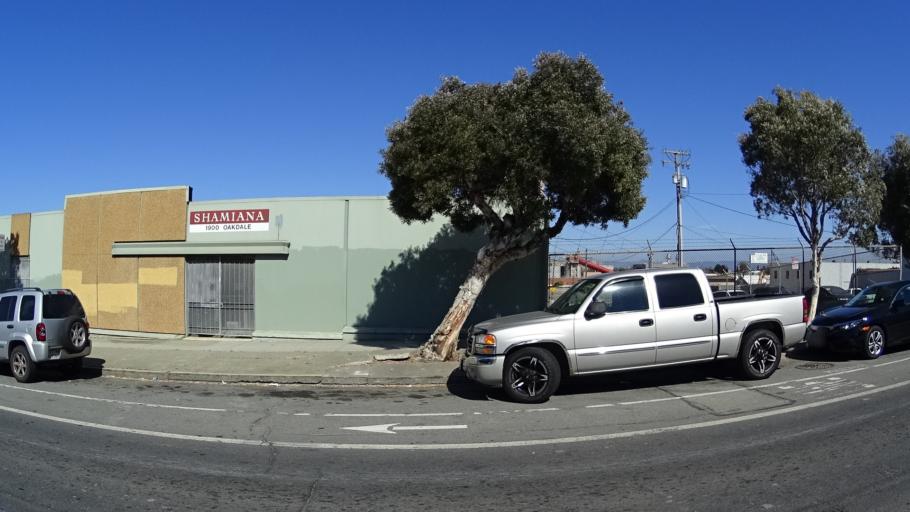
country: US
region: California
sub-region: San Francisco County
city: San Francisco
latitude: 37.7379
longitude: -122.3962
